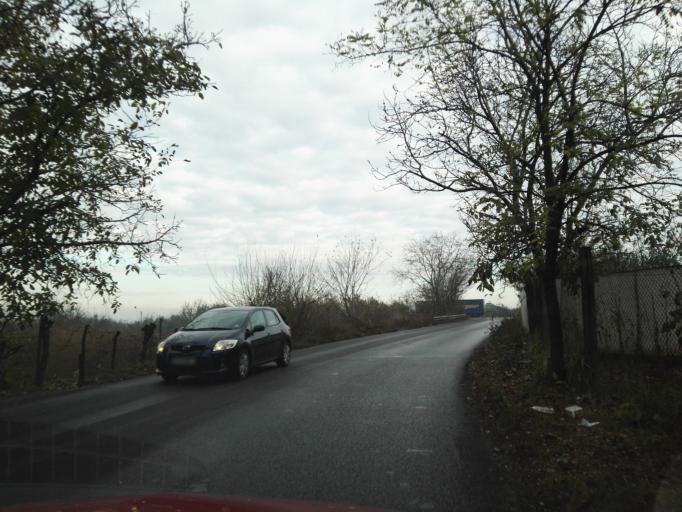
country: RO
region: Ilfov
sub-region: Comuna Jilava
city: Jilava
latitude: 44.3430
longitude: 26.0808
